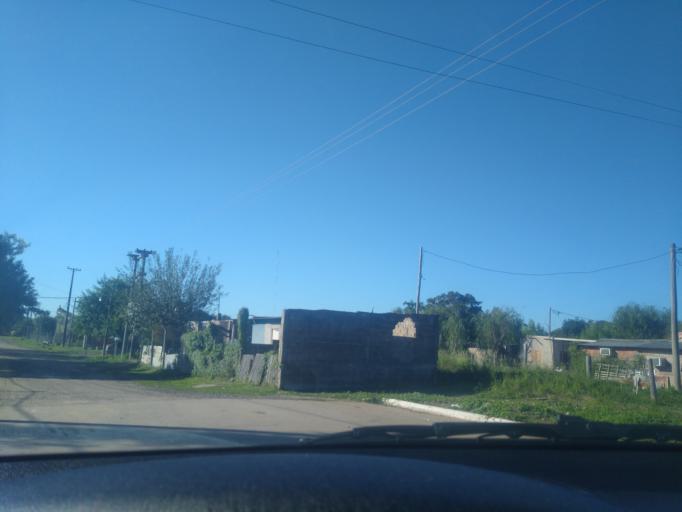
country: AR
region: Chaco
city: Puerto Vilelas
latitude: -27.5094
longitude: -58.9372
